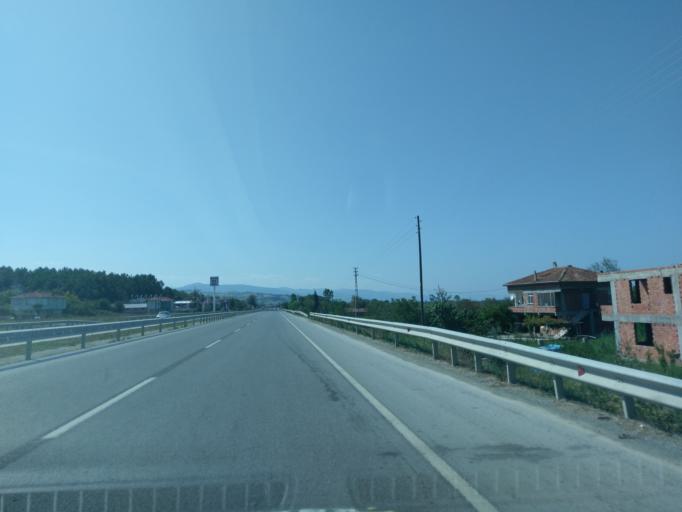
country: TR
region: Samsun
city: Alacam
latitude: 41.6085
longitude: 35.6829
